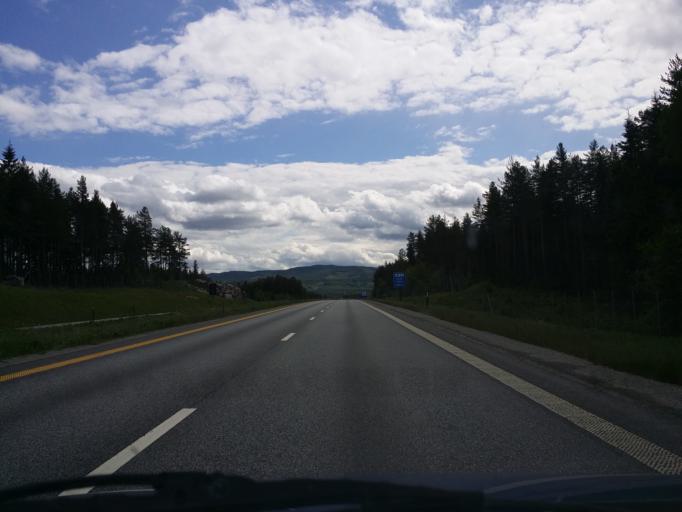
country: NO
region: Hedmark
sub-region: Stange
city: Stange
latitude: 60.6463
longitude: 11.2944
